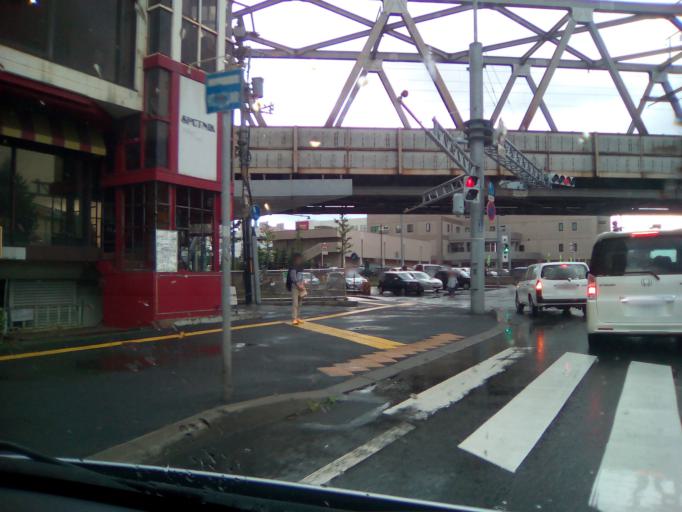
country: JP
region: Hokkaido
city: Ebetsu
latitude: 43.0398
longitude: 141.4699
